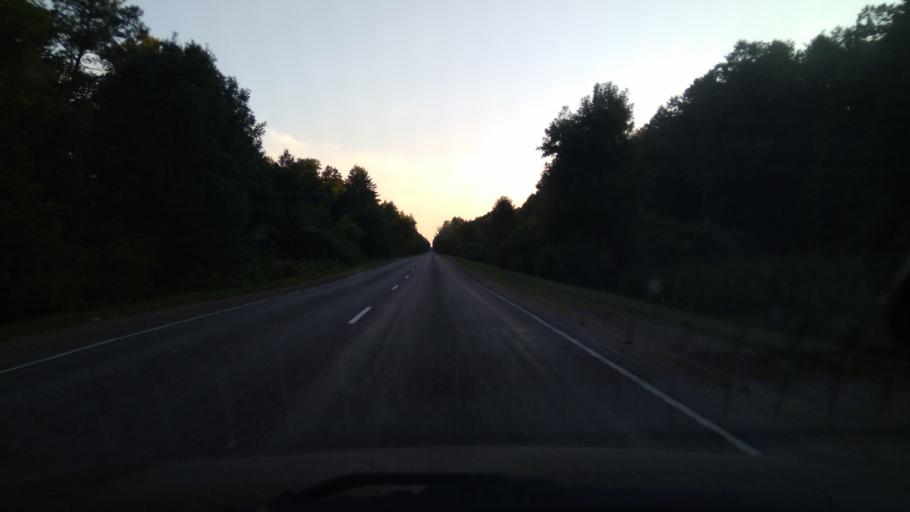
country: BY
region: Brest
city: Nyakhachava
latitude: 52.6135
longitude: 25.1439
